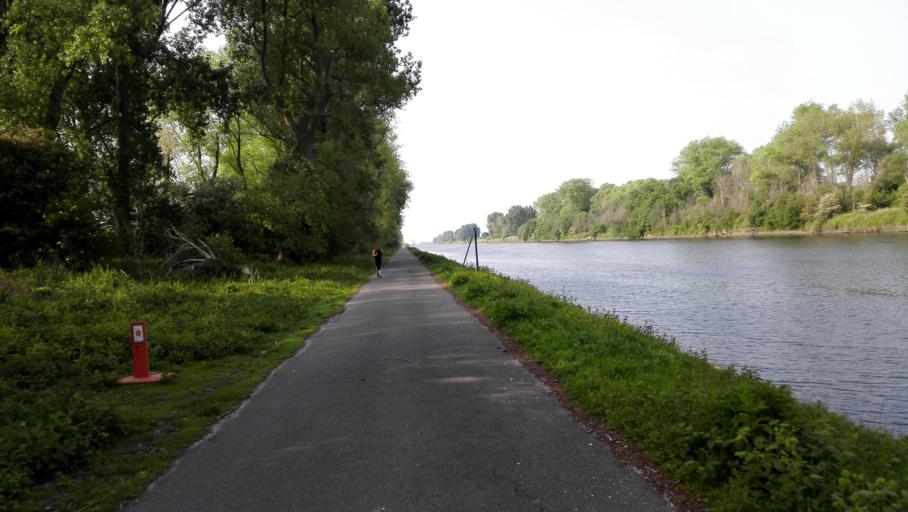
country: BE
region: Flanders
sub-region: Provincie West-Vlaanderen
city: Zeebrugge
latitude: 51.2858
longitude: 3.2083
